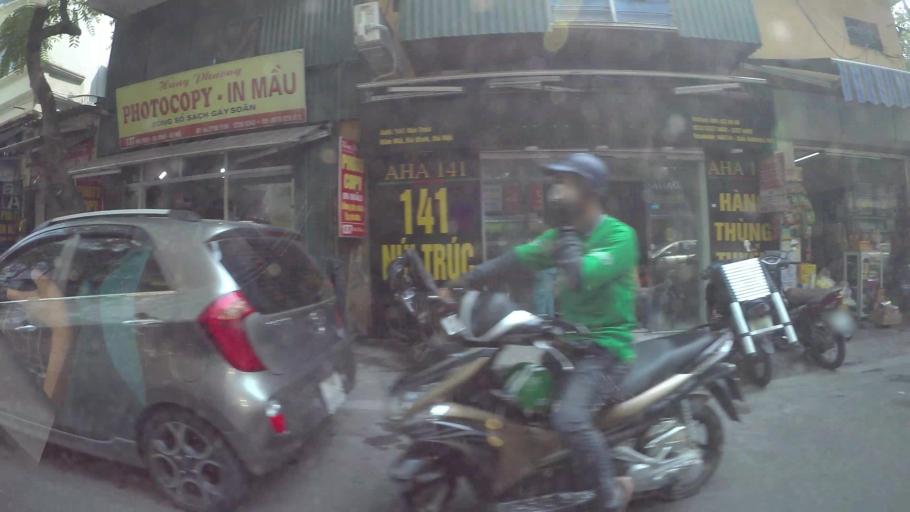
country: VN
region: Ha Noi
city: Dong Da
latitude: 21.0285
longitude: 105.8241
